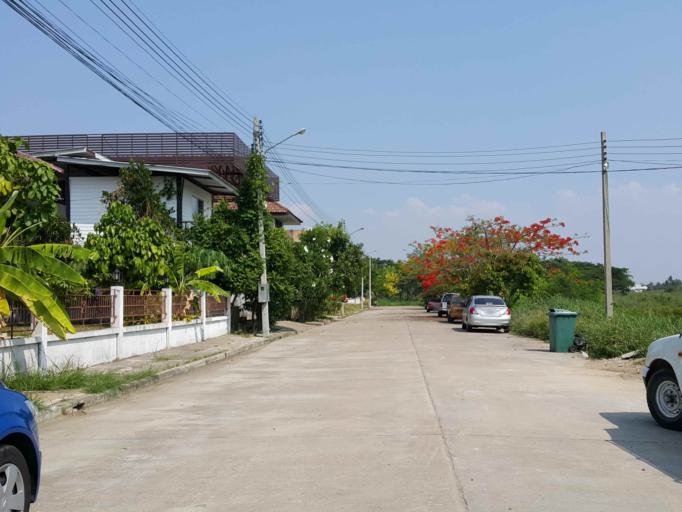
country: TH
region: Chiang Mai
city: Saraphi
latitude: 18.7528
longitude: 99.0430
